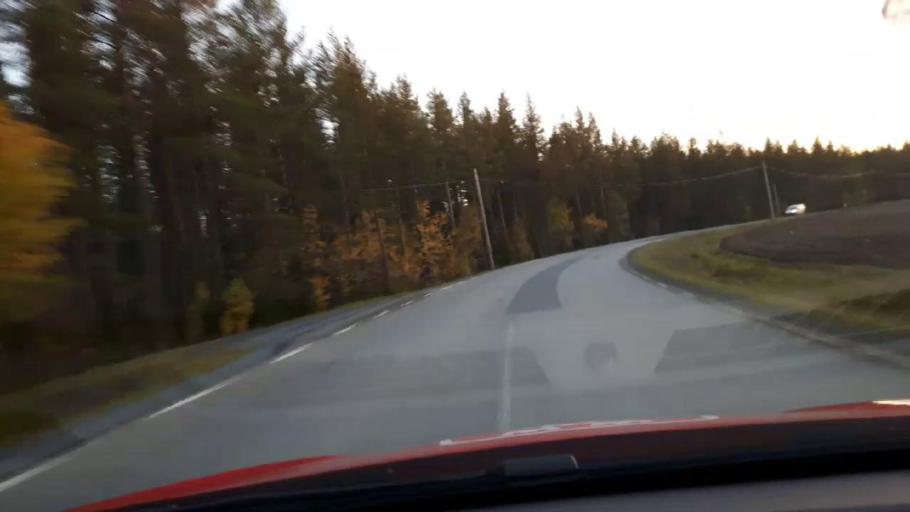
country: SE
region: Jaemtland
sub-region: OEstersunds Kommun
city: Ostersund
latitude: 63.2492
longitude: 14.5998
